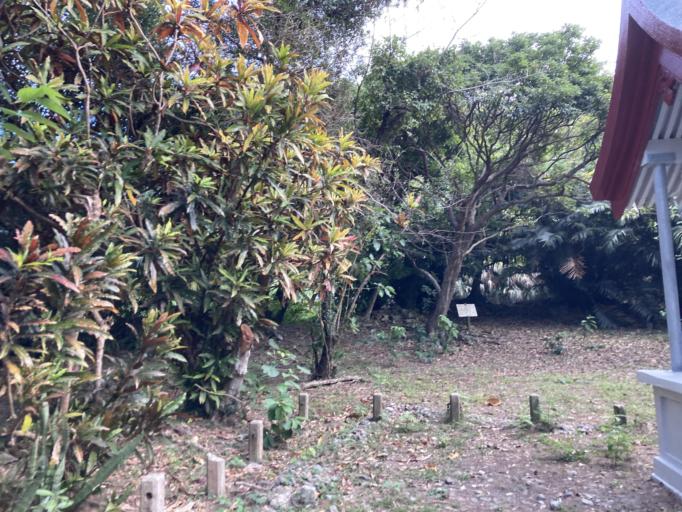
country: JP
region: Okinawa
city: Ginowan
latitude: 26.1657
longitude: 127.7874
